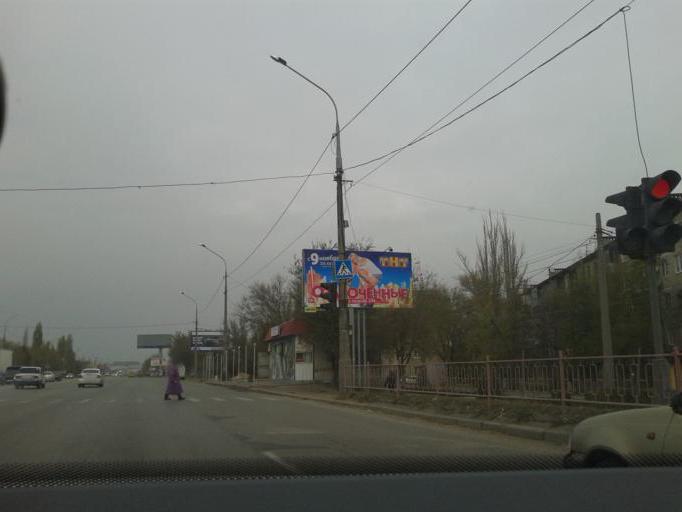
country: RU
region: Volgograd
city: Volgograd
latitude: 48.7578
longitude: 44.4798
